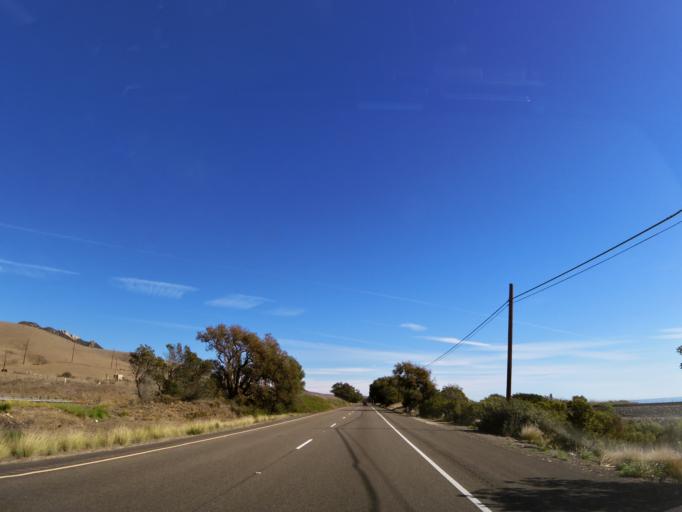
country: US
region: California
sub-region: Santa Barbara County
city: Solvang
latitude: 34.4714
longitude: -120.1796
